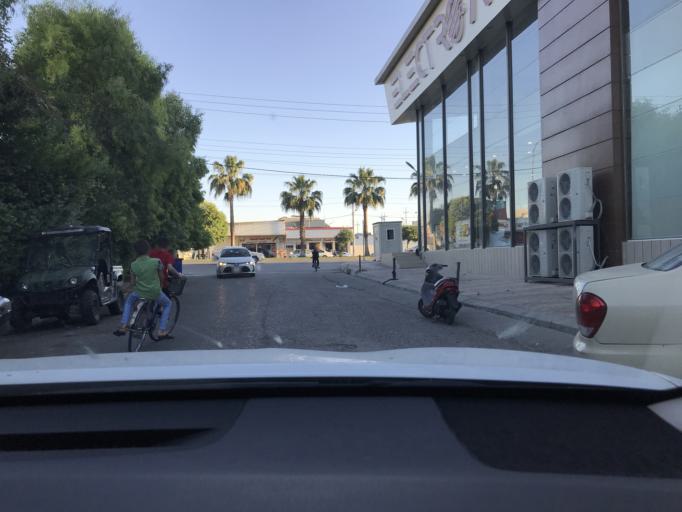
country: IQ
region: Arbil
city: Erbil
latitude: 36.2041
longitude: 44.0127
